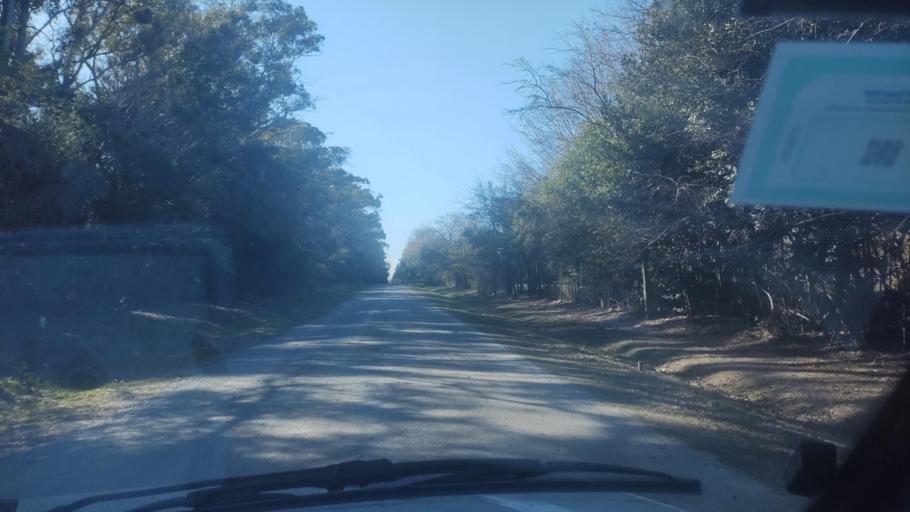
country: AR
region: Buenos Aires
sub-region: Partido de La Plata
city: La Plata
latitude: -34.8533
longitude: -58.1061
